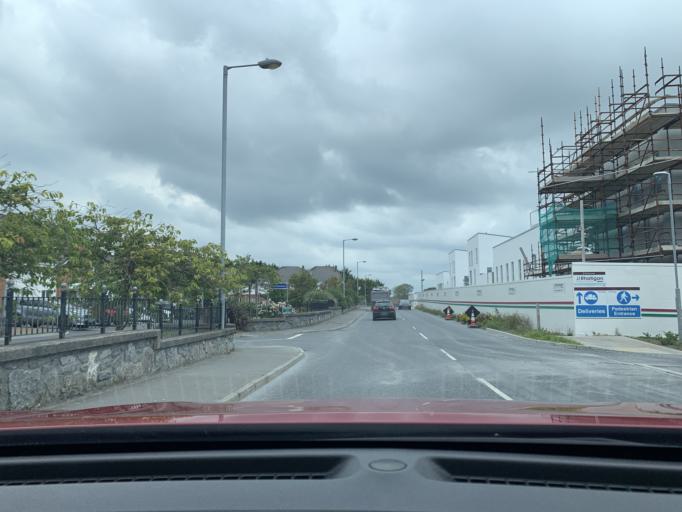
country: IE
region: Connaught
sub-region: County Galway
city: Bearna
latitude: 53.2737
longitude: -9.1177
